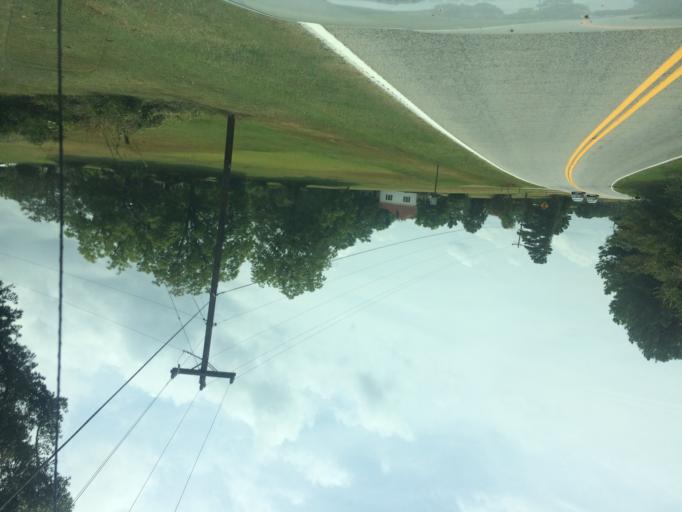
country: US
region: South Carolina
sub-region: Anderson County
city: Centerville
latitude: 34.5327
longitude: -82.8035
